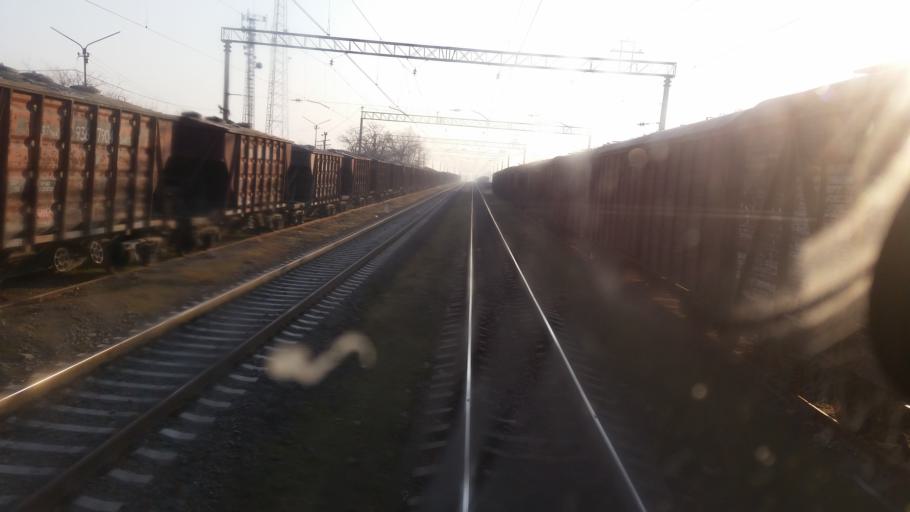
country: AZ
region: Yevlax
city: Aran
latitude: 40.6372
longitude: 47.0003
